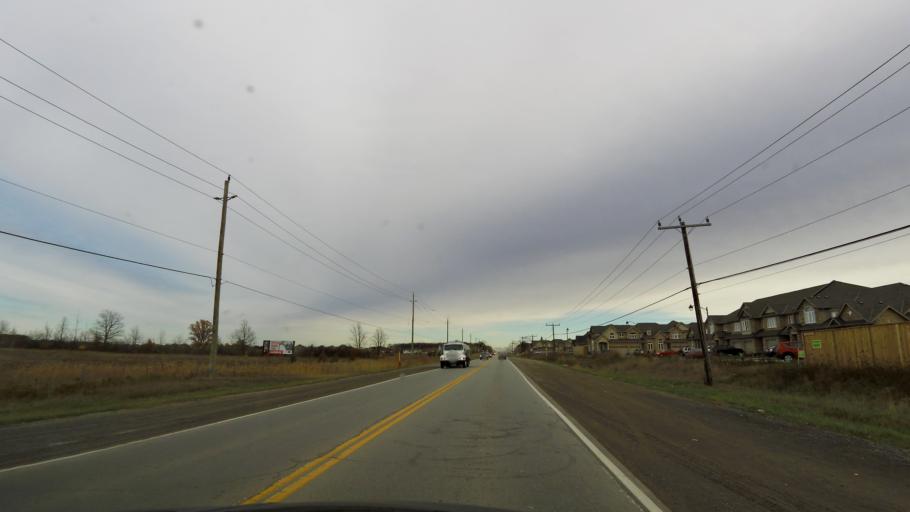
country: CA
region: Ontario
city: Hamilton
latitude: 43.1790
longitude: -79.8022
